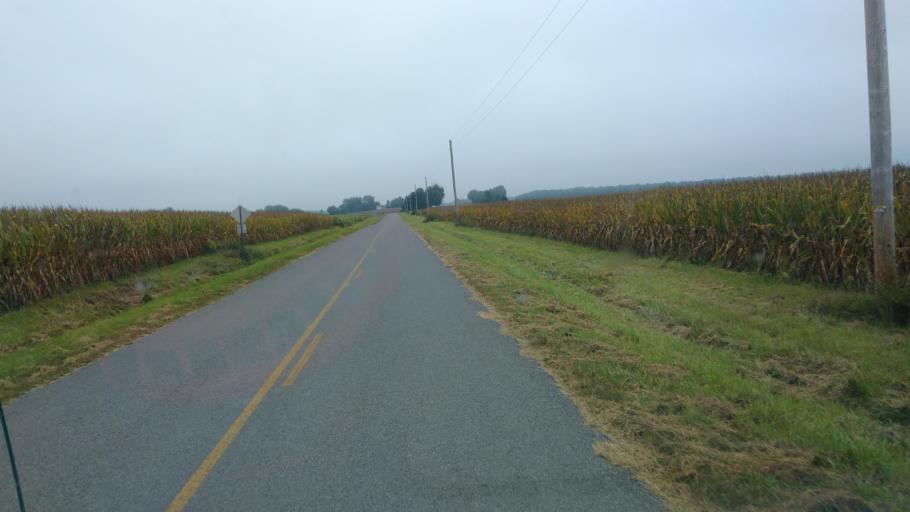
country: US
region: Ohio
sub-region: Logan County
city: Northwood
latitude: 40.4791
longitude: -83.5833
